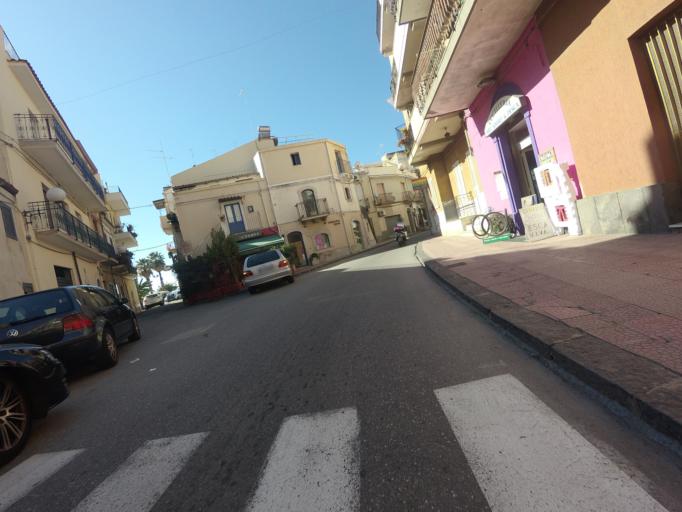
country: IT
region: Sicily
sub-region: Messina
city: Taormina
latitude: 37.8422
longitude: 15.2797
